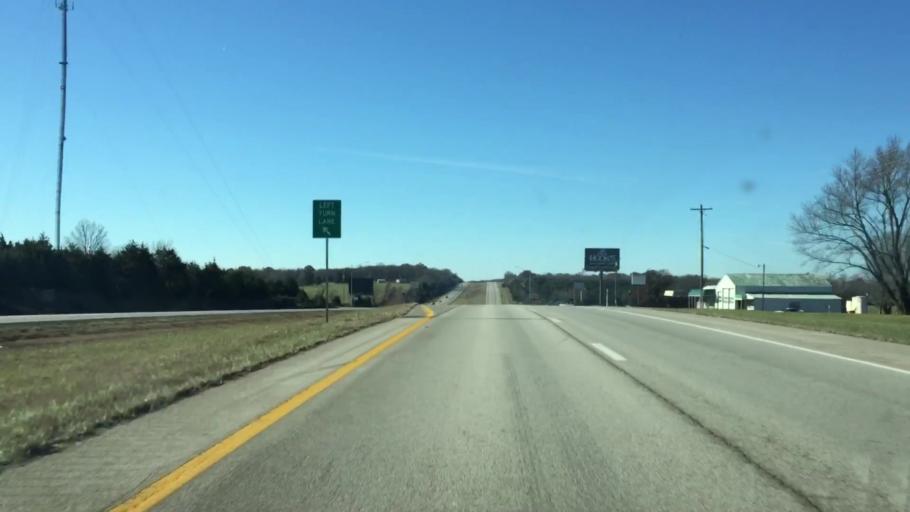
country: US
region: Missouri
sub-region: Cole County
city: Saint Martins
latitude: 38.4144
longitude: -92.3471
